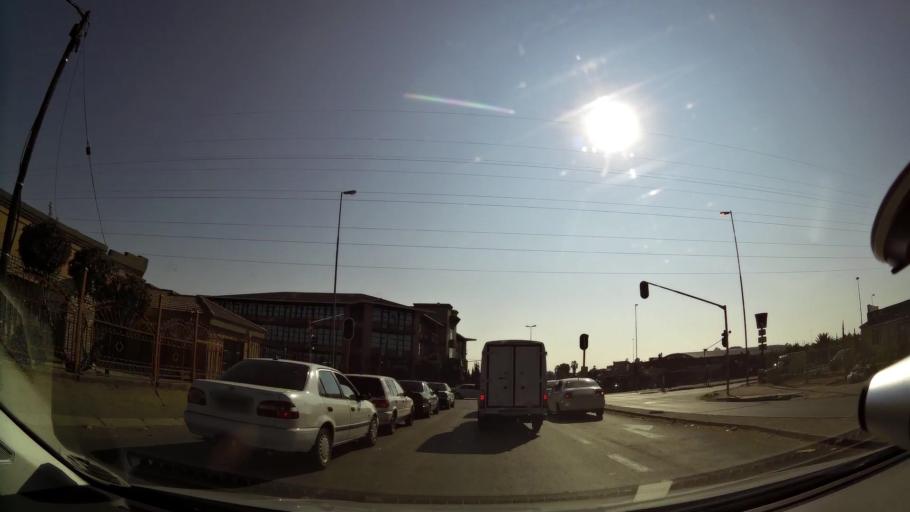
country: ZA
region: Orange Free State
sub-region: Mangaung Metropolitan Municipality
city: Bloemfontein
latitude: -29.1702
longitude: 26.2355
